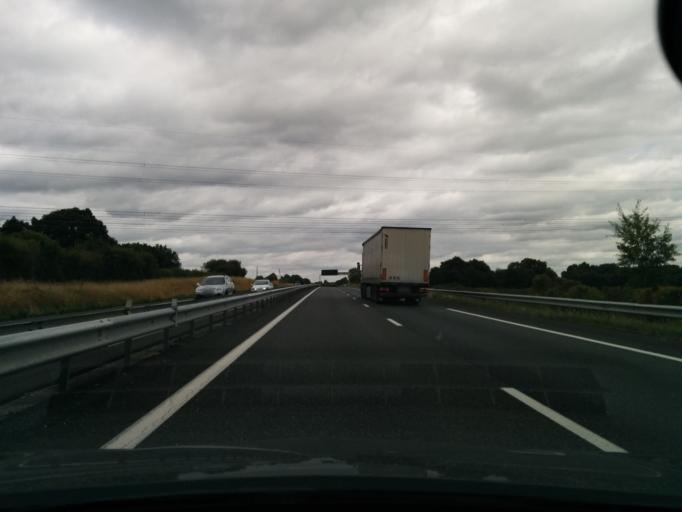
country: FR
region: Centre
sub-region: Departement de l'Indre
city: Chantome
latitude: 46.4736
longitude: 1.4976
